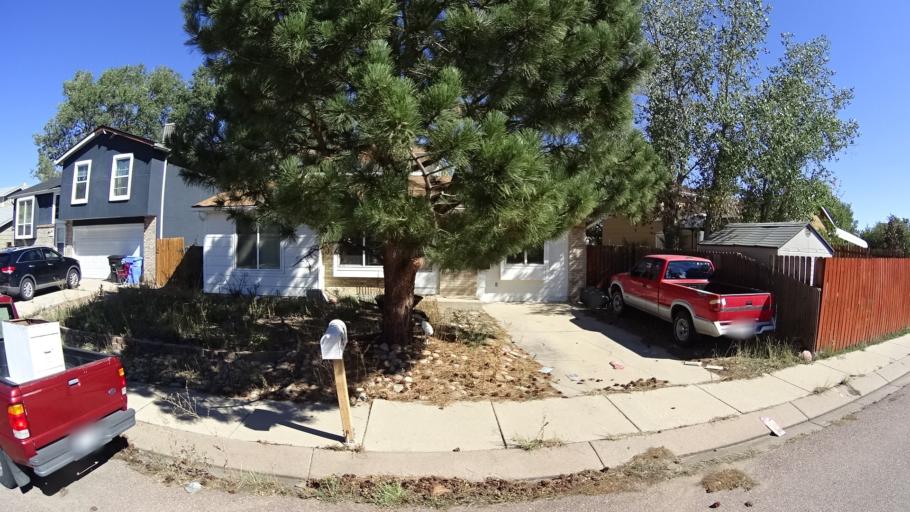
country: US
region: Colorado
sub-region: El Paso County
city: Cimarron Hills
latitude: 38.8191
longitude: -104.7374
